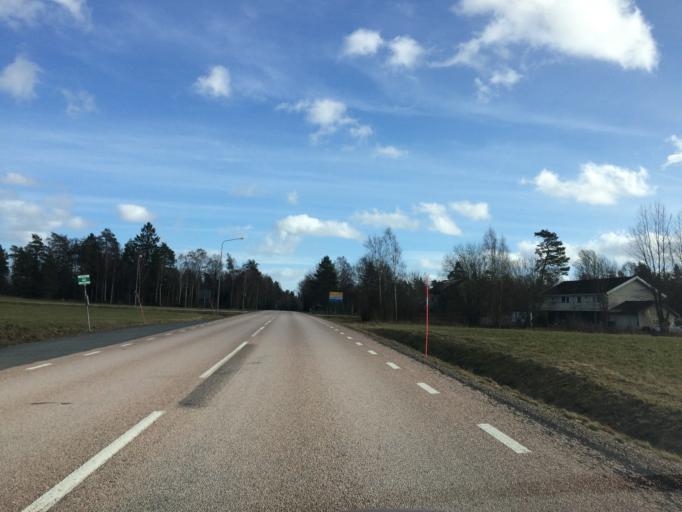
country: SE
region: Kronoberg
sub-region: Markaryds Kommun
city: Stromsnasbruk
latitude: 56.7900
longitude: 13.5656
